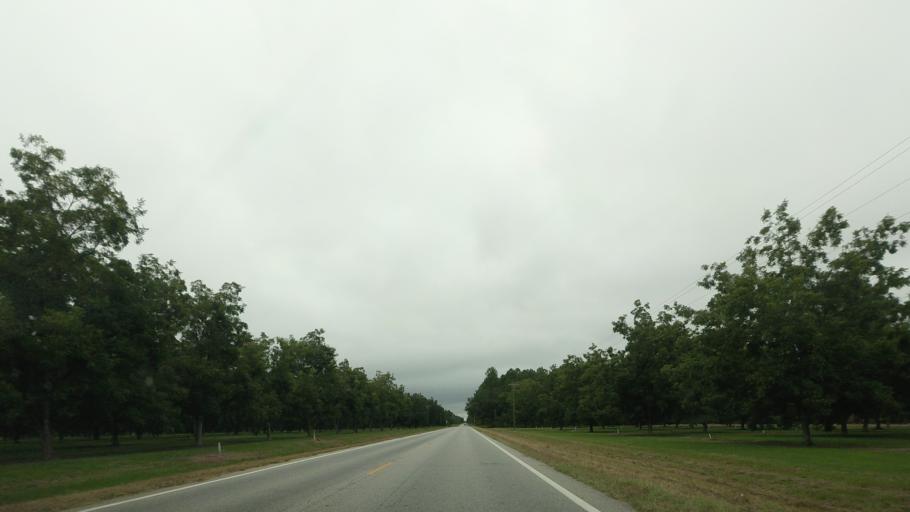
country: US
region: Georgia
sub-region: Berrien County
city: Ray City
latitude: 31.0970
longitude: -83.2071
